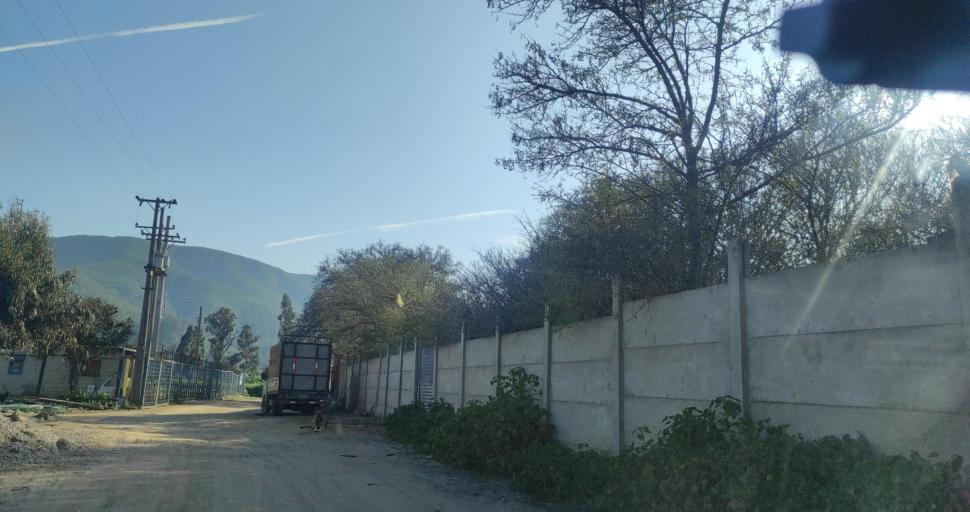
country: CL
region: Valparaiso
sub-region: Provincia de Marga Marga
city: Limache
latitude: -33.0015
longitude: -71.2531
